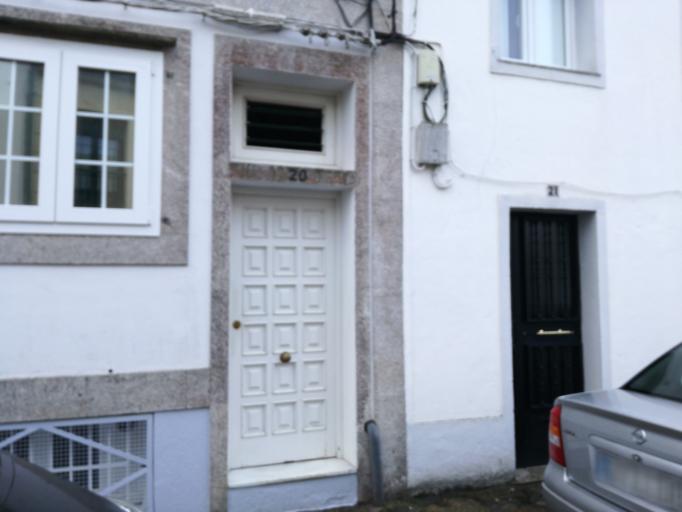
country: ES
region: Galicia
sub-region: Provincia da Coruna
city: Santiago de Compostela
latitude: 42.8796
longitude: -8.5360
